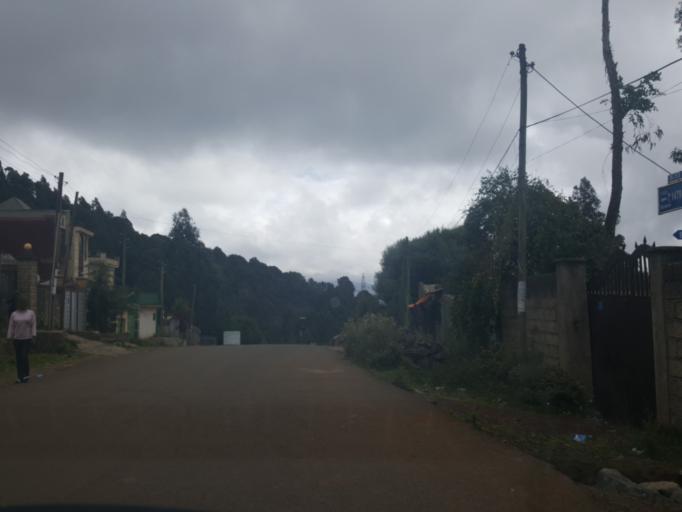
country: ET
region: Adis Abeba
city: Addis Ababa
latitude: 9.0678
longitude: 38.7420
